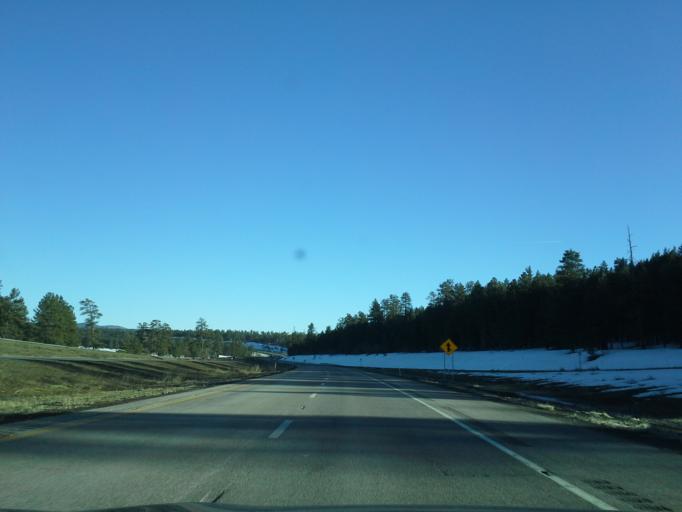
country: US
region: Arizona
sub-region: Coconino County
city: Sedona
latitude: 34.8744
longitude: -111.6348
